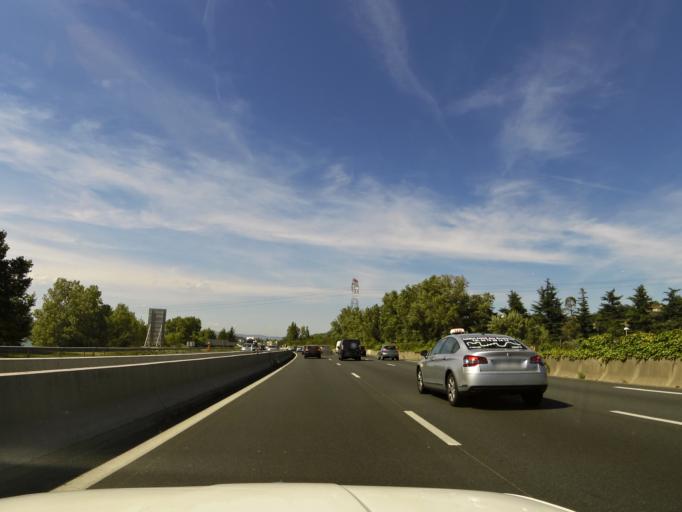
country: FR
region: Rhone-Alpes
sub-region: Departement de l'Isere
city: Chasse-sur-Rhone
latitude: 45.5679
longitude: 4.8165
